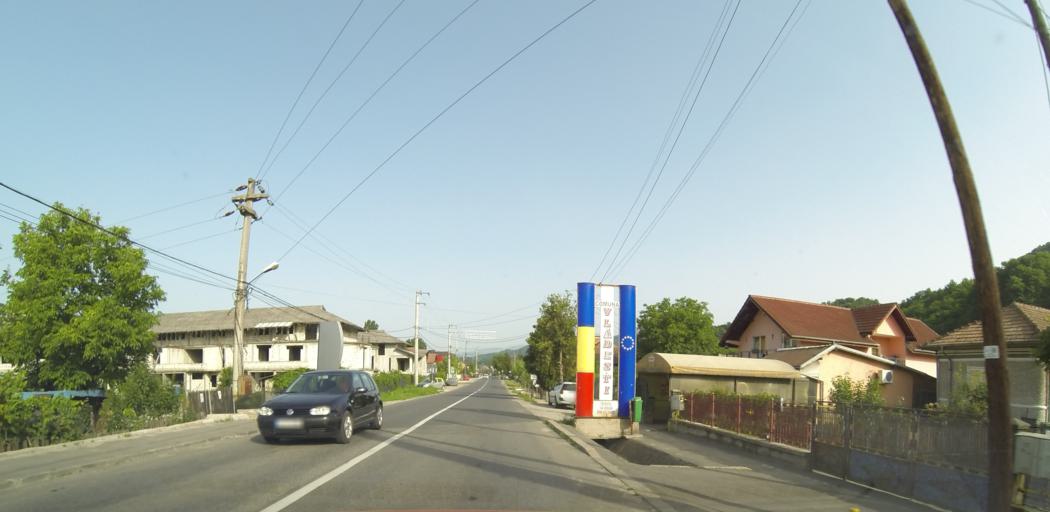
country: RO
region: Valcea
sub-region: Comuna Vladesti
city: Vladesti
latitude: 45.1139
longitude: 24.3215
